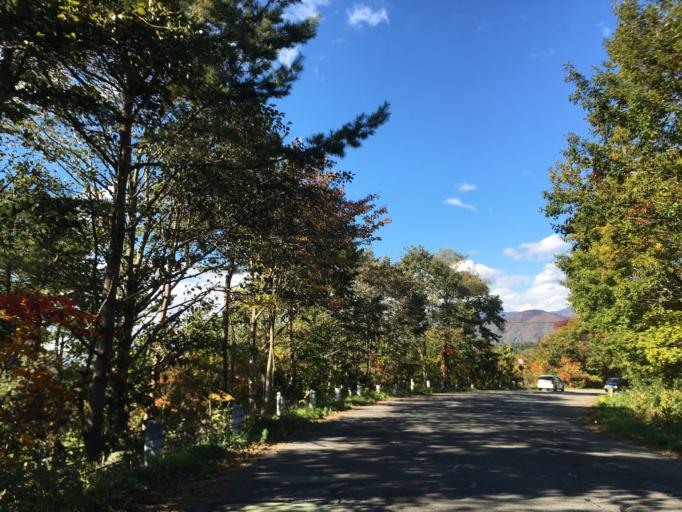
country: JP
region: Fukushima
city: Inawashiro
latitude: 37.6088
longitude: 140.2300
